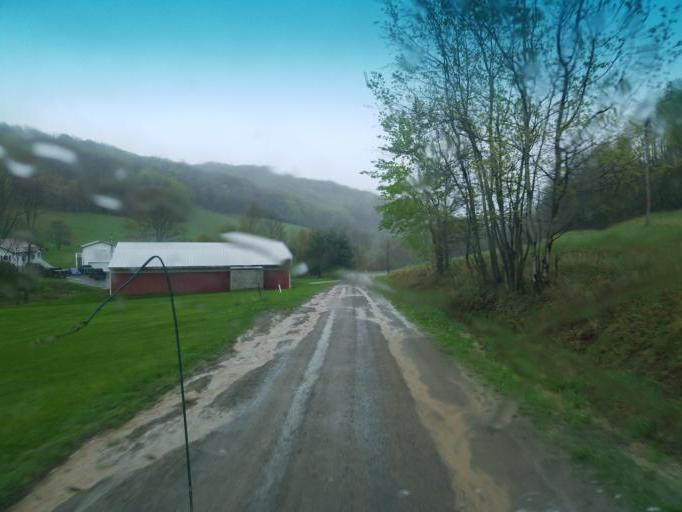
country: US
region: Pennsylvania
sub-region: Tioga County
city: Westfield
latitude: 41.9136
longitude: -77.6468
